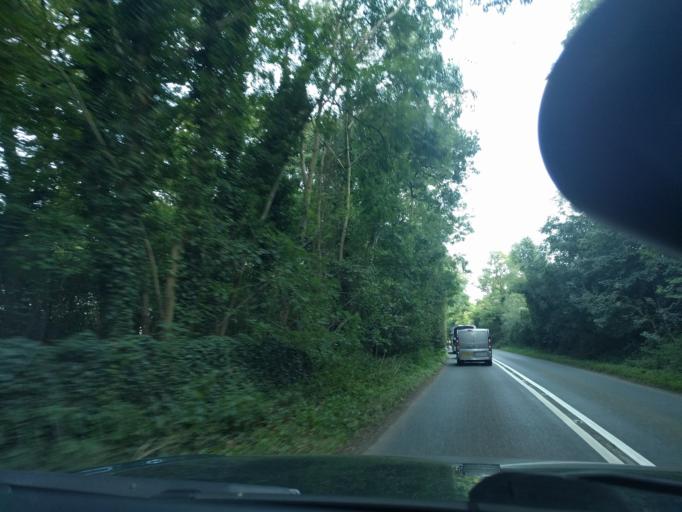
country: GB
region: England
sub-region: Wiltshire
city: Neston
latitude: 51.3989
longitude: -2.2096
